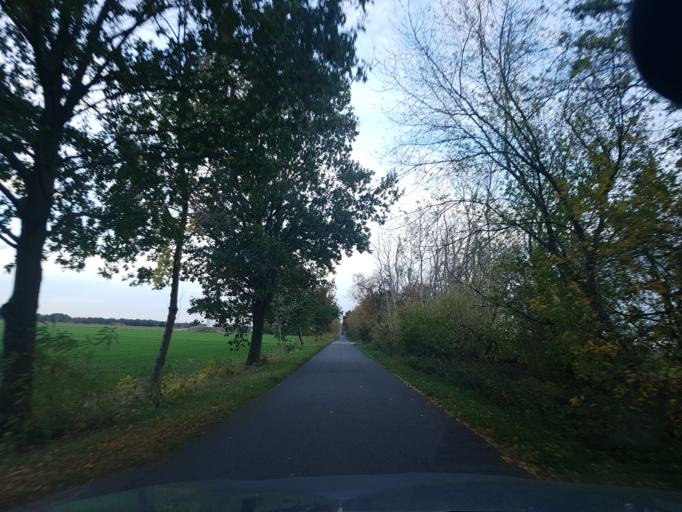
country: DE
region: Brandenburg
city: Elsterwerda
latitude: 51.4553
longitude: 13.4730
